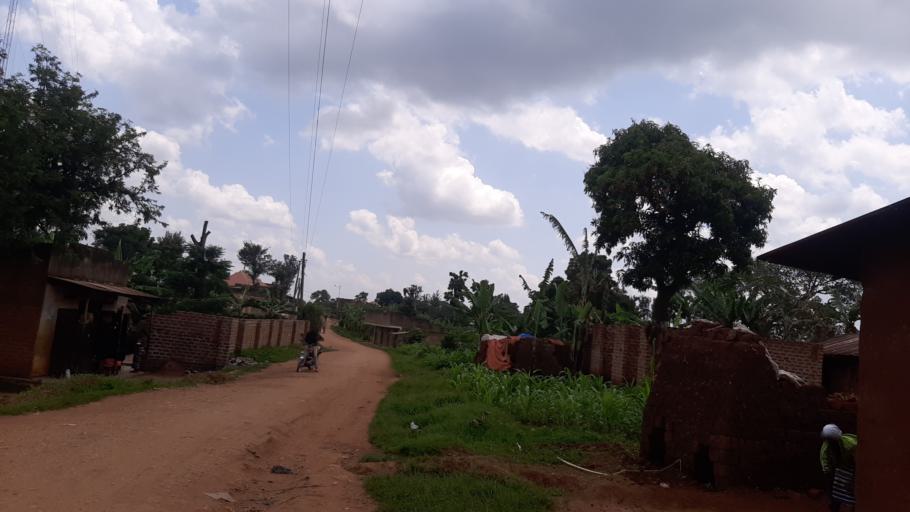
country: UG
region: Eastern Region
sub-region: Mbale District
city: Mbale
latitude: 1.0602
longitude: 34.2081
